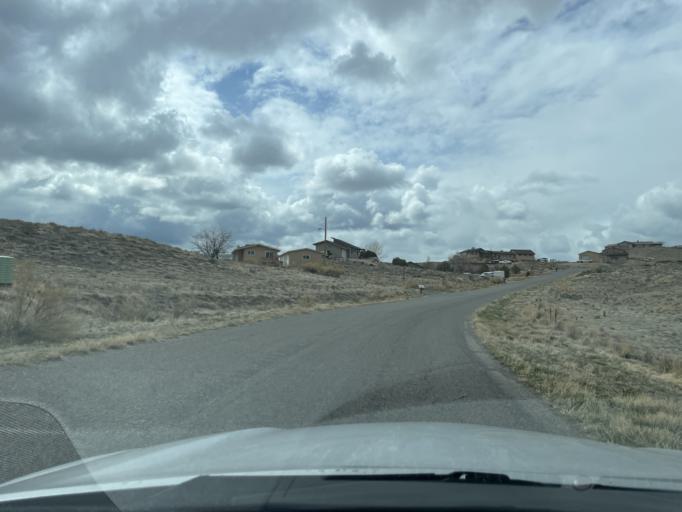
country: US
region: Colorado
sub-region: Mesa County
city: Redlands
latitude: 39.0584
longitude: -108.5989
